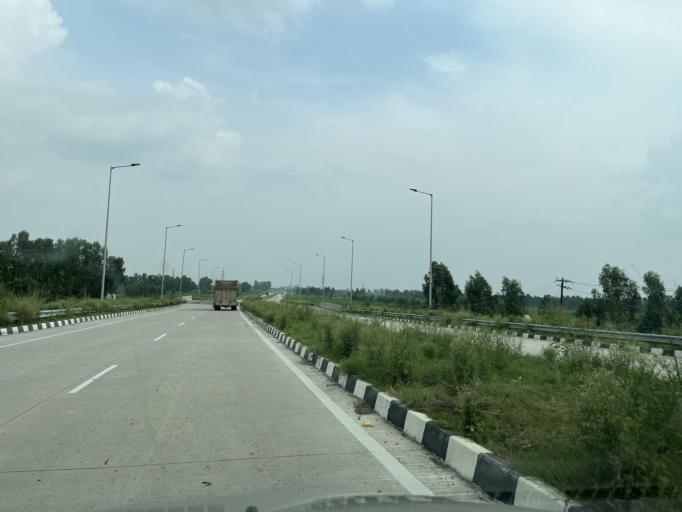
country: IN
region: Uttarakhand
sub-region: Udham Singh Nagar
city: Kashipur
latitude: 29.1719
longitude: 78.9500
